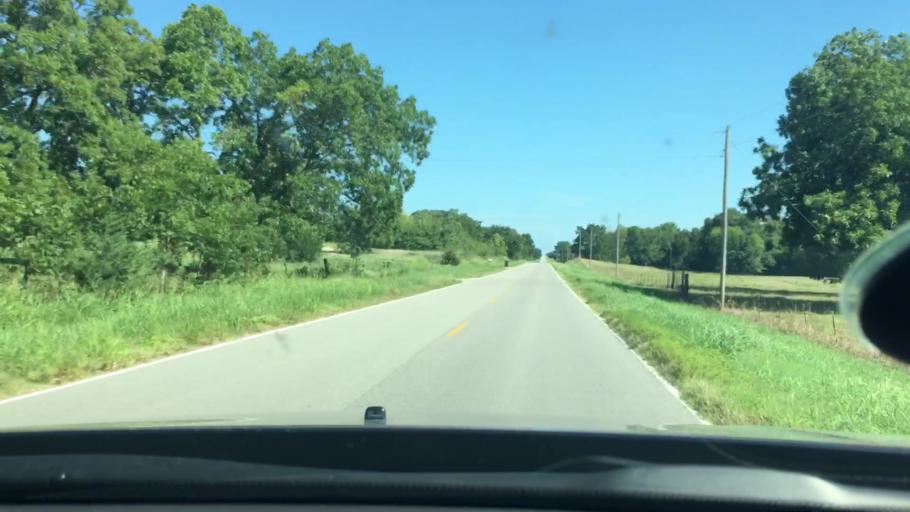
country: US
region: Oklahoma
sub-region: Johnston County
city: Tishomingo
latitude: 34.2843
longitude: -96.5487
